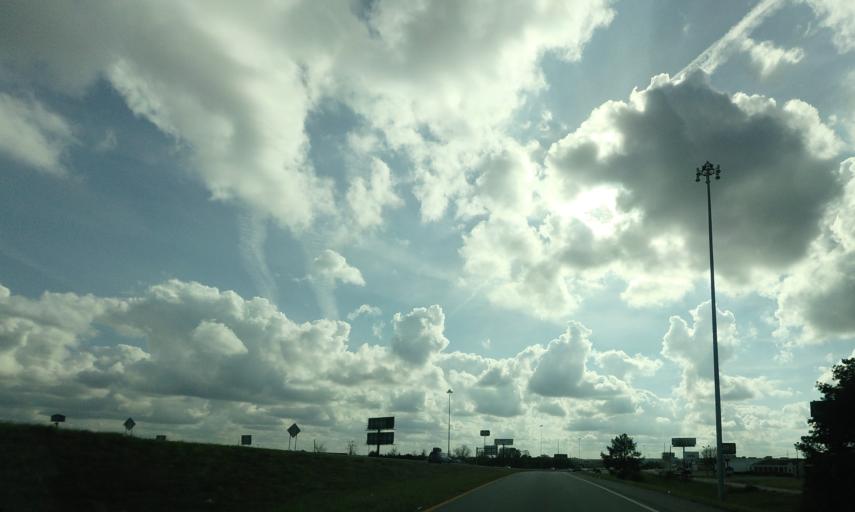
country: US
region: Georgia
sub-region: Houston County
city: Perry
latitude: 32.4702
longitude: -83.7448
